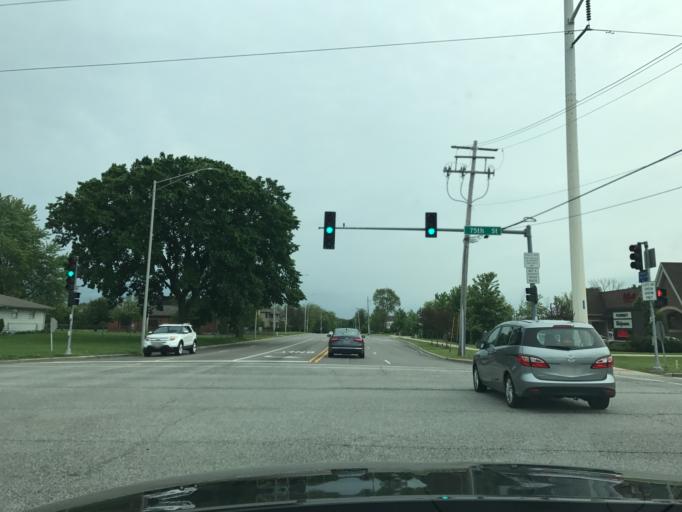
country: US
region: Illinois
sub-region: DuPage County
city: Woodridge
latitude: 41.7492
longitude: -88.1037
